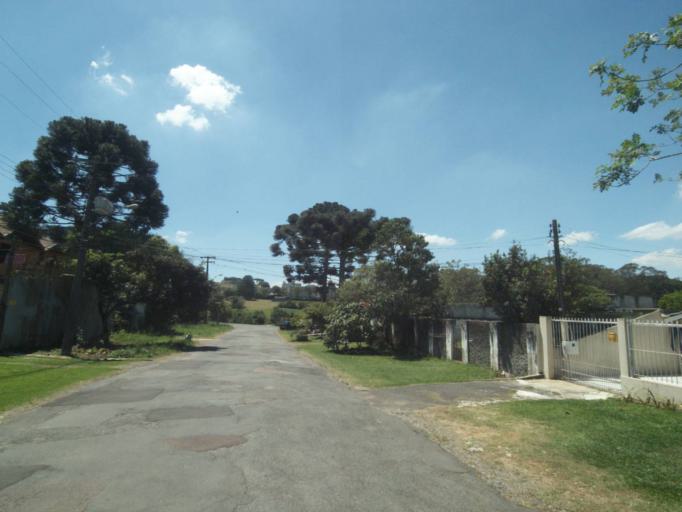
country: BR
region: Parana
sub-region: Curitiba
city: Curitiba
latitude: -25.3872
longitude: -49.2263
